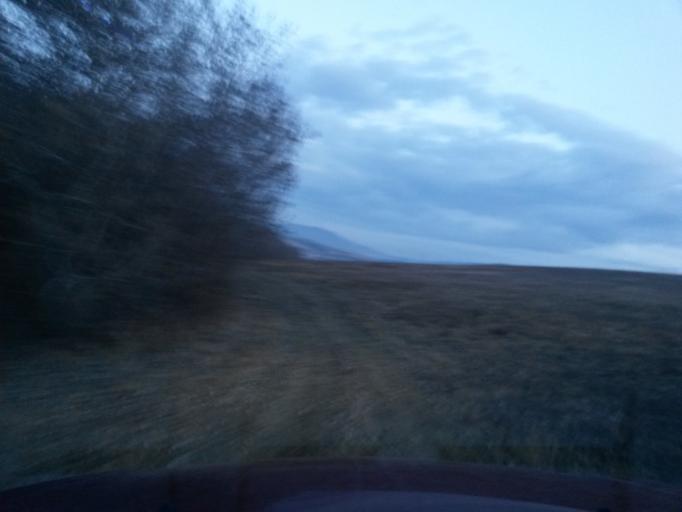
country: SK
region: Kosicky
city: Kosice
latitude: 48.7025
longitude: 21.3130
